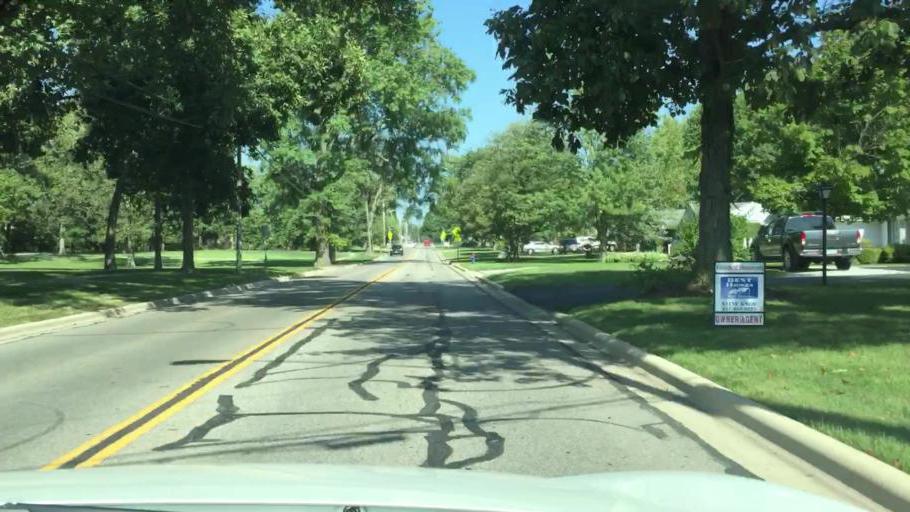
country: US
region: Ohio
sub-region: Union County
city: Marysville
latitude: 40.2295
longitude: -83.3848
